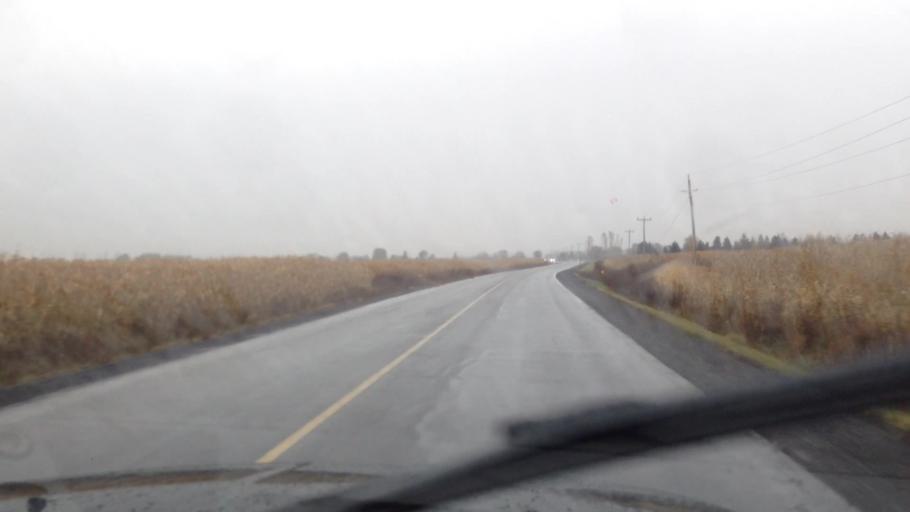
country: CA
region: Ontario
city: Bourget
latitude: 45.2888
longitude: -75.2784
